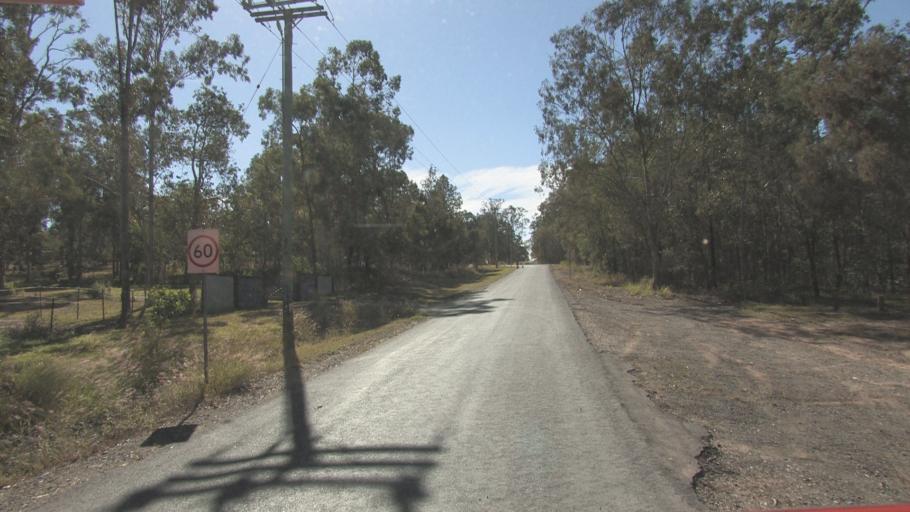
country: AU
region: Queensland
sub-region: Ipswich
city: Springfield Lakes
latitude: -27.7054
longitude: 152.9685
